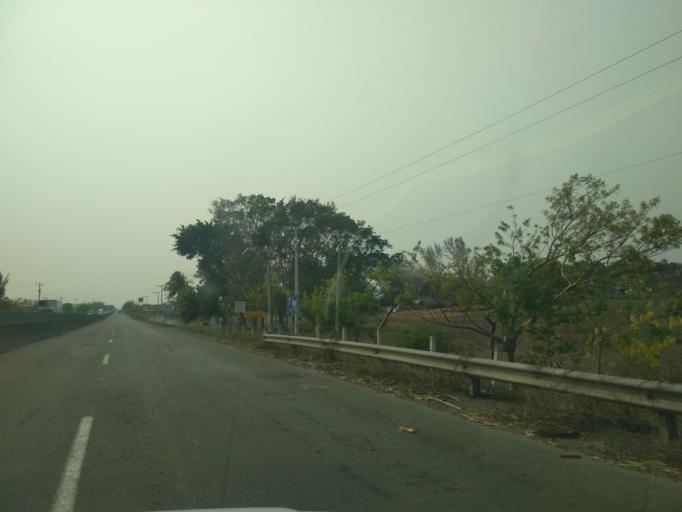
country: MX
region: Veracruz
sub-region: Veracruz
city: Las Amapolas
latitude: 19.1165
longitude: -96.2321
